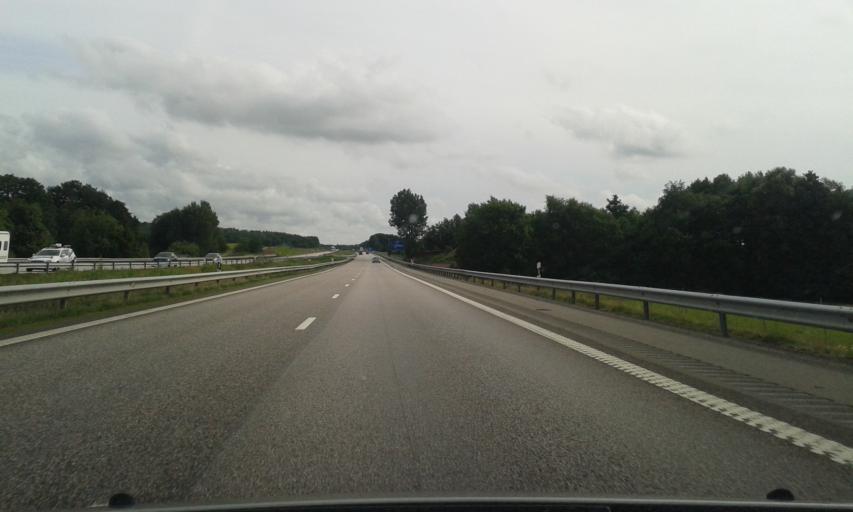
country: SE
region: Halland
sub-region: Kungsbacka Kommun
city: Frillesas
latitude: 57.2615
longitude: 12.2158
